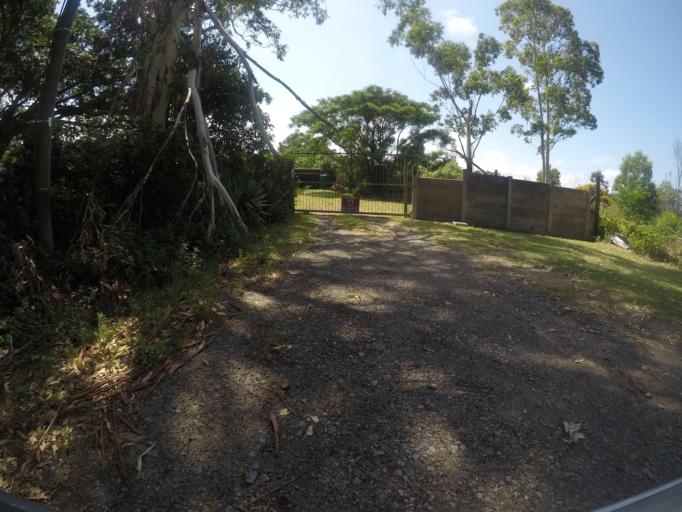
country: ZA
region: Eastern Cape
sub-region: Buffalo City Metropolitan Municipality
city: East London
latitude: -32.9691
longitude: 27.8580
